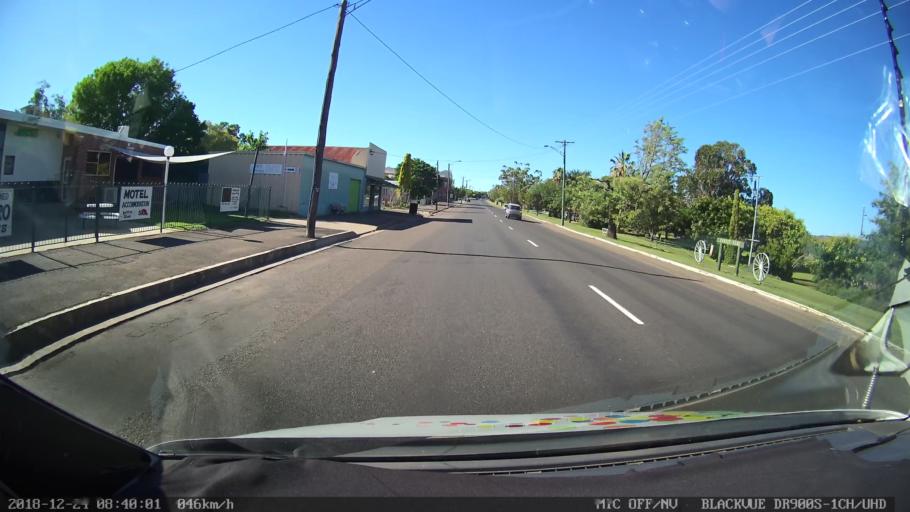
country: AU
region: New South Wales
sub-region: Liverpool Plains
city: Quirindi
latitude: -31.3519
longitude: 150.6470
